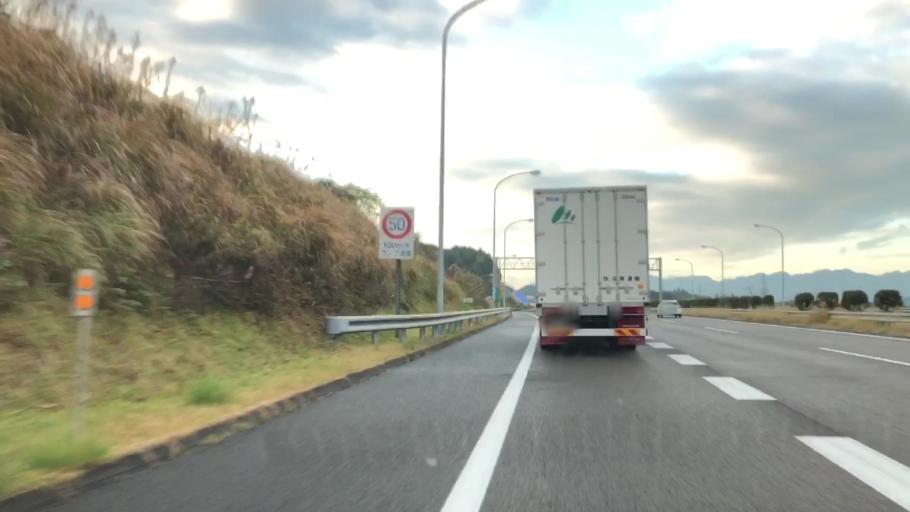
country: JP
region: Saga Prefecture
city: Ureshinomachi-shimojuku
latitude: 33.1502
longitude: 129.9998
